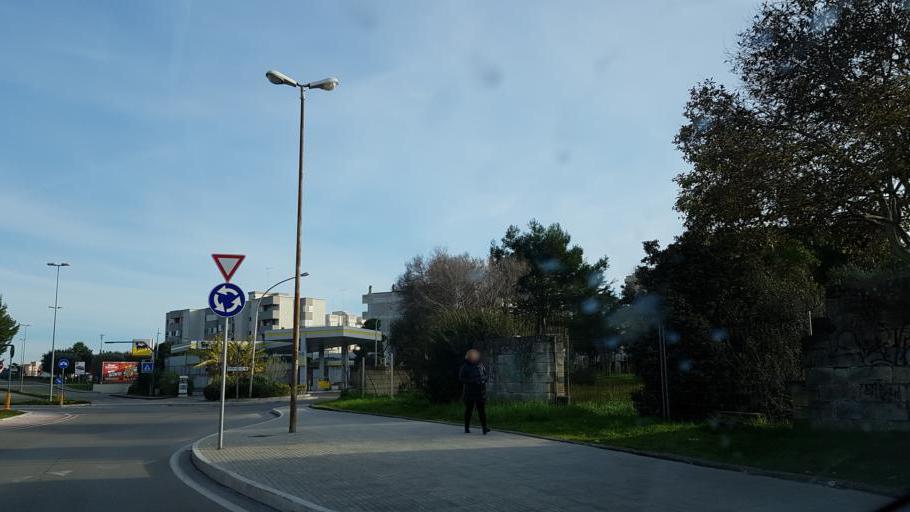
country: IT
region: Apulia
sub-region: Provincia di Brindisi
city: Brindisi
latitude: 40.6274
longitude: 17.9407
